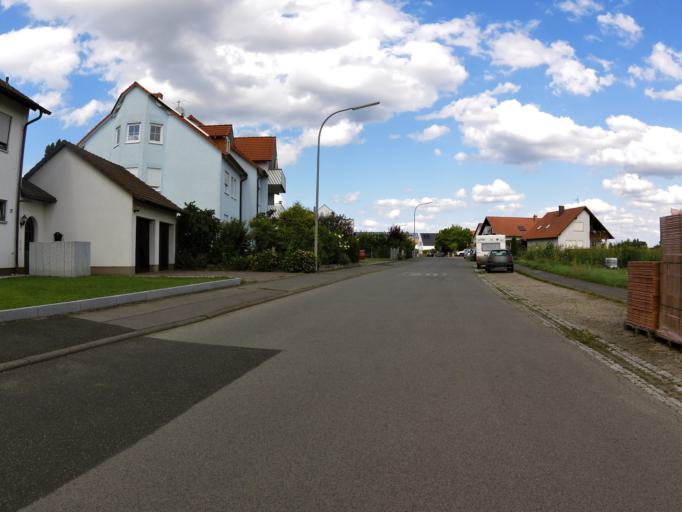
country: DE
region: Bavaria
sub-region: Regierungsbezirk Unterfranken
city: Bergrheinfeld
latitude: 50.0117
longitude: 10.1866
